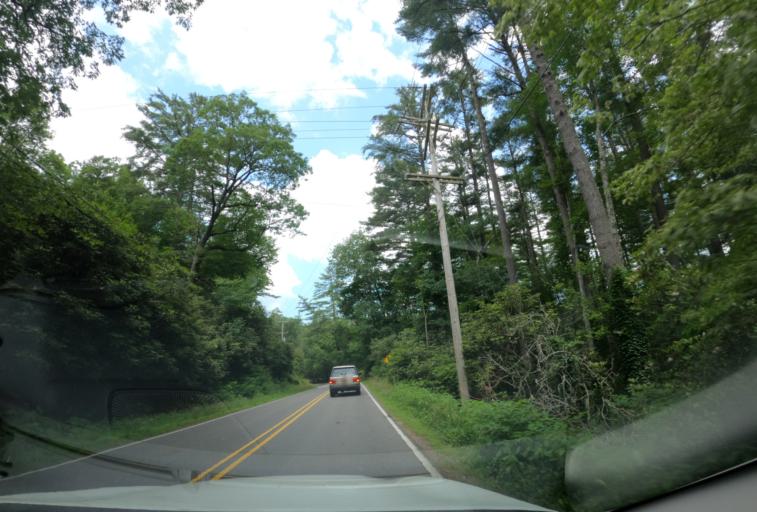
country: US
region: North Carolina
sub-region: Macon County
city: Franklin
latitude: 35.0622
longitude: -83.2105
